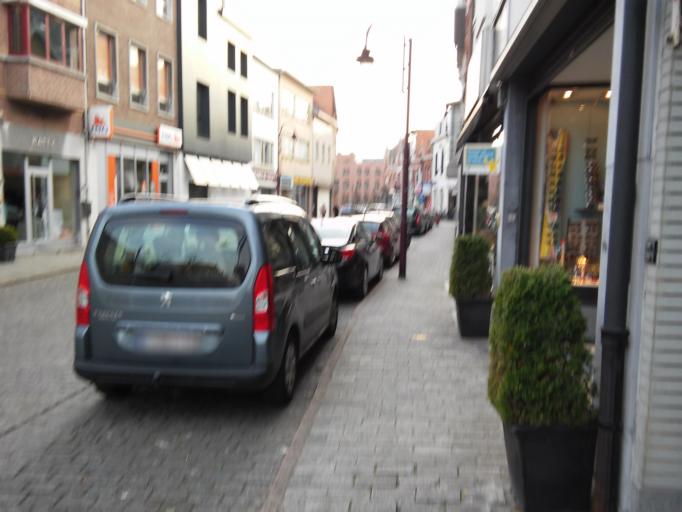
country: BE
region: Flanders
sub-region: Provincie Antwerpen
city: Duffel
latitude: 51.0953
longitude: 4.5013
